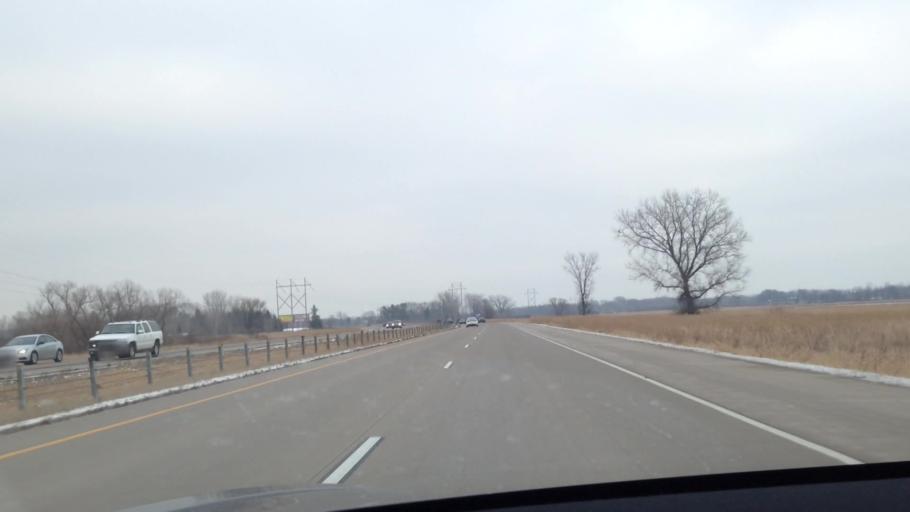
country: US
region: Minnesota
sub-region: Anoka County
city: Centerville
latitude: 45.1959
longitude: -93.0614
